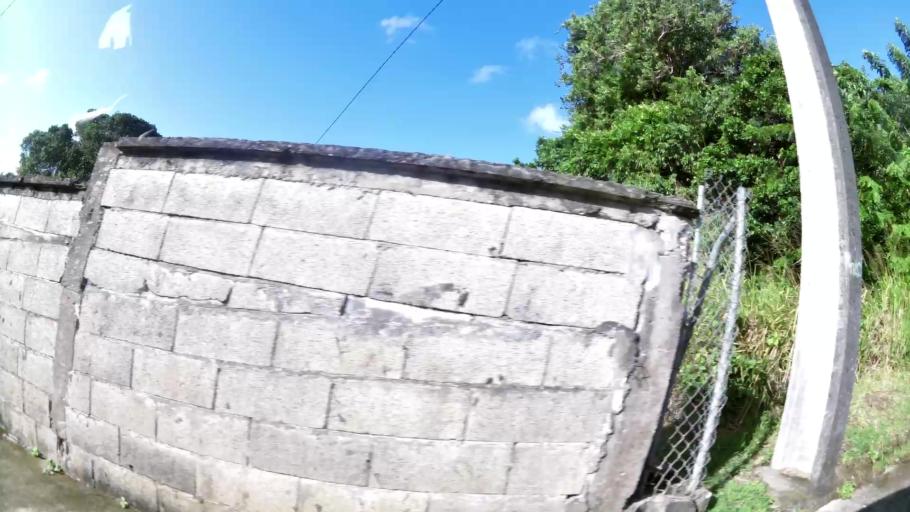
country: MQ
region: Martinique
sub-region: Martinique
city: Le Lamentin
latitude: 14.6250
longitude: -61.0245
